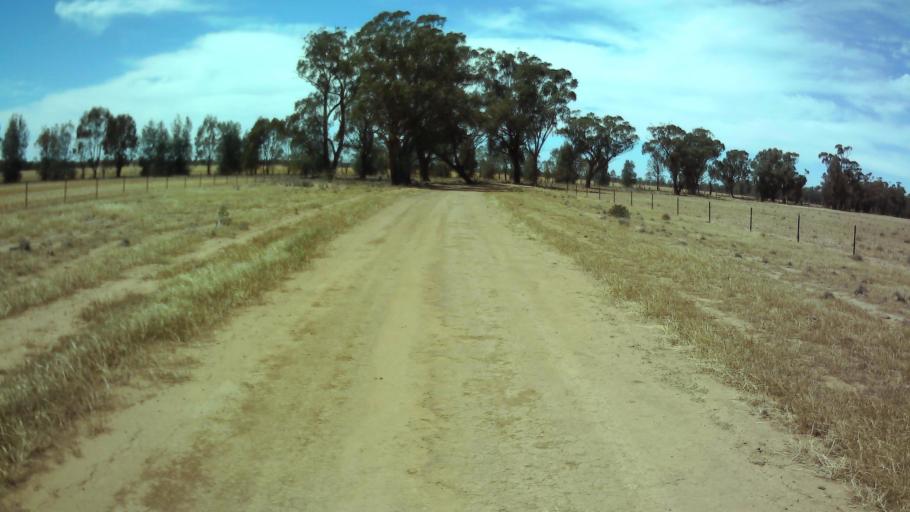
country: AU
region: New South Wales
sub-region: Weddin
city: Grenfell
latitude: -33.9032
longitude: 147.8071
